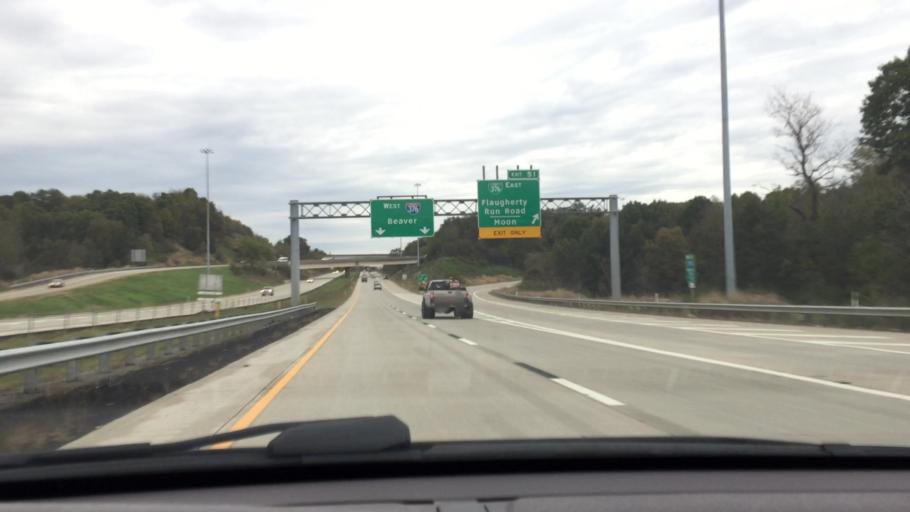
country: US
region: Pennsylvania
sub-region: Allegheny County
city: Carnot-Moon
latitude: 40.5087
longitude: -80.2804
